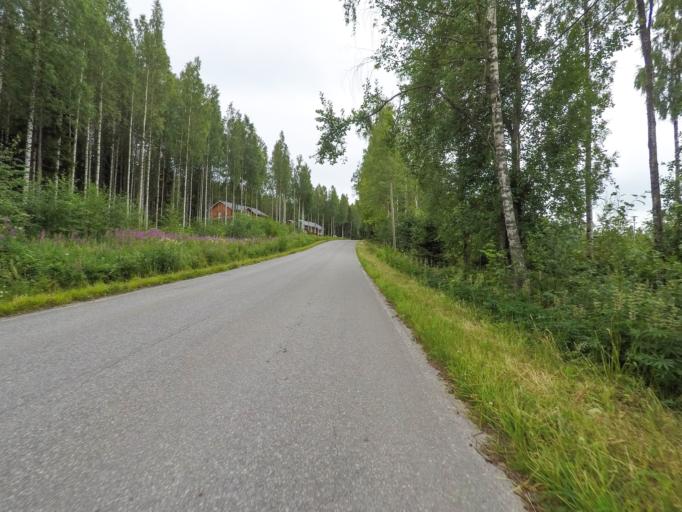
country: FI
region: Uusimaa
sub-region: Helsinki
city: Karjalohja
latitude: 60.2570
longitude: 23.7410
